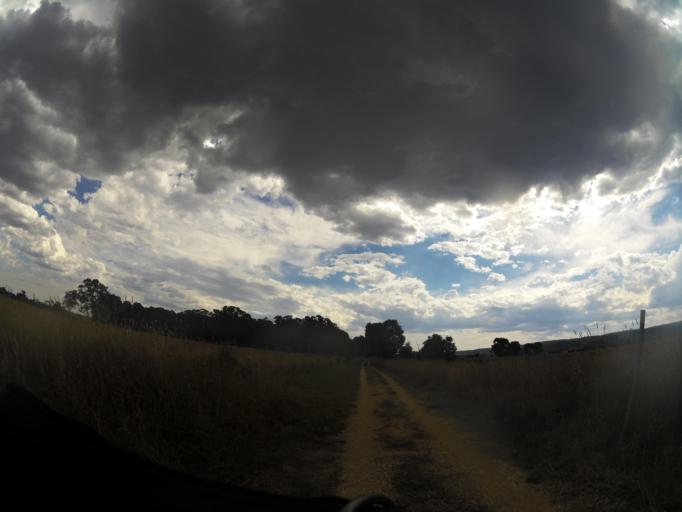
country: AU
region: Victoria
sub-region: Wellington
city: Heyfield
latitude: -38.0162
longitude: 146.6889
